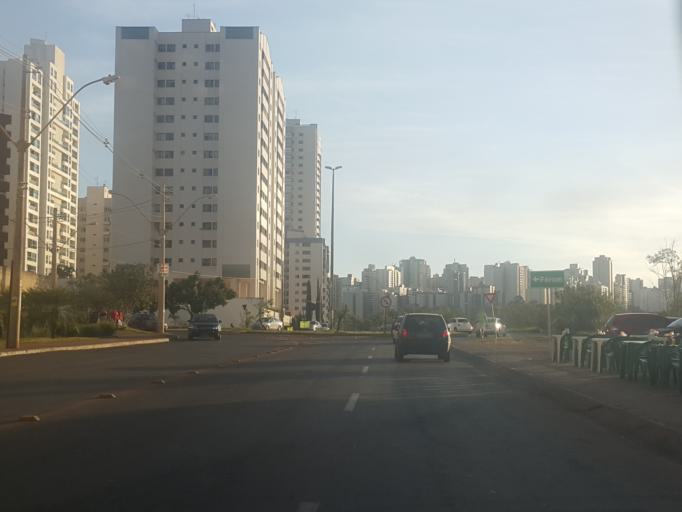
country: BR
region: Federal District
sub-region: Brasilia
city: Brasilia
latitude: -15.8323
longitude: -48.0174
